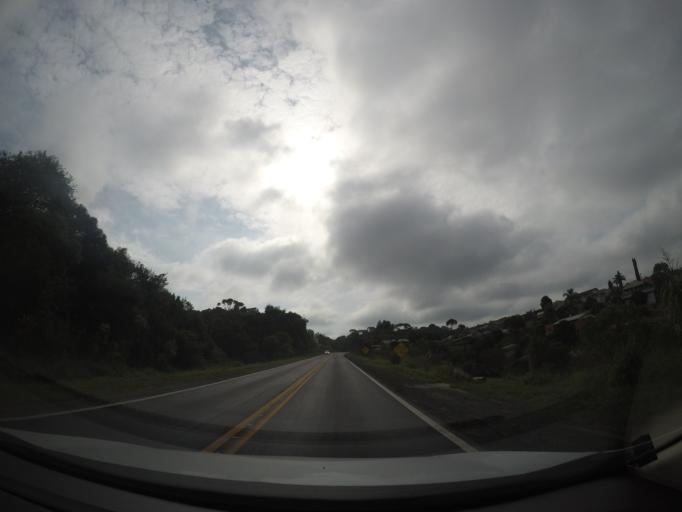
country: BR
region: Parana
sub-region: Colombo
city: Colombo
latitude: -25.3430
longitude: -49.2271
